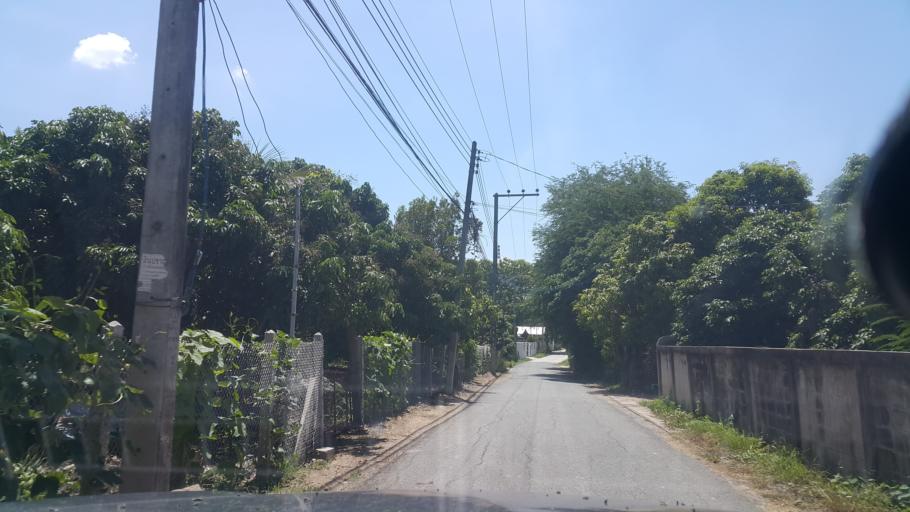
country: TH
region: Chiang Mai
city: San Kamphaeng
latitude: 18.7006
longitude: 99.1593
